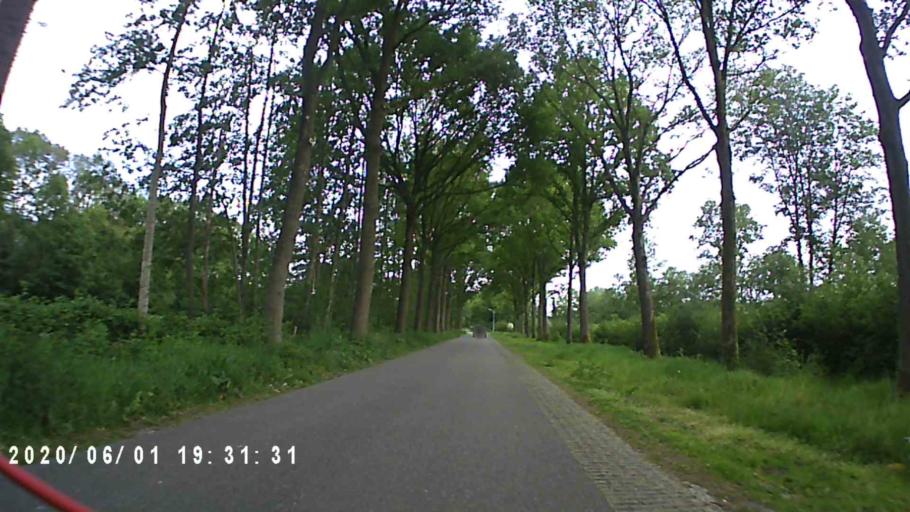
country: NL
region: Friesland
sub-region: Gemeente Achtkarspelen
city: Augustinusga
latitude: 53.2148
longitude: 6.1574
